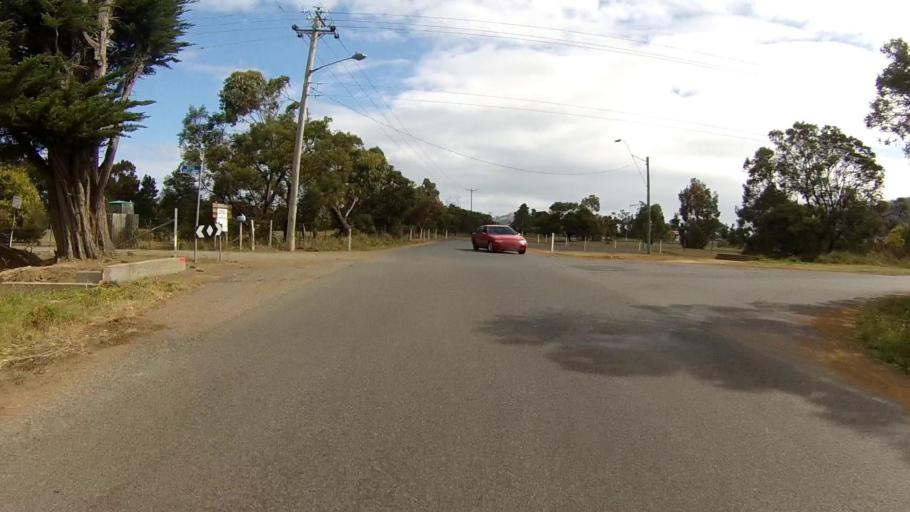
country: AU
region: Tasmania
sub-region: Clarence
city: Acton Park
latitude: -42.8895
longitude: 147.4962
